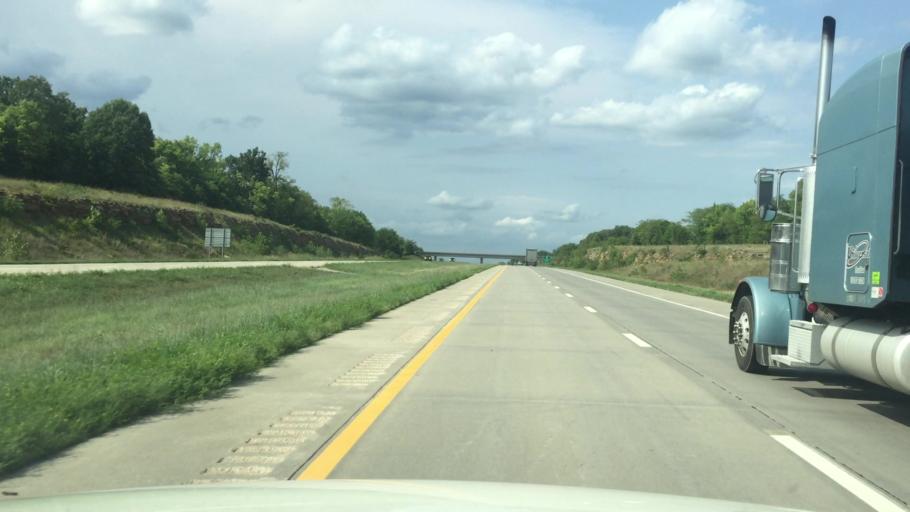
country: US
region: Kansas
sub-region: Miami County
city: Louisburg
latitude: 38.6014
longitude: -94.6940
